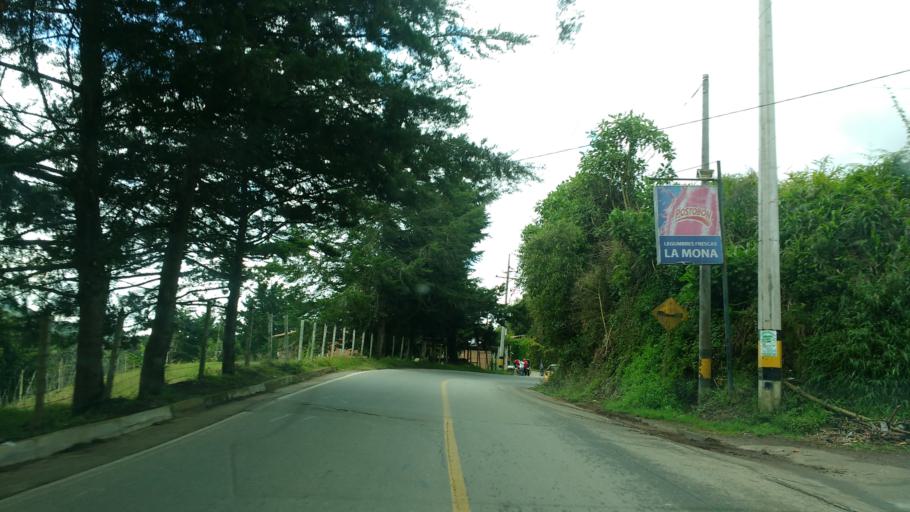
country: CO
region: Antioquia
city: Marinilla
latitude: 6.1868
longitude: -75.2916
